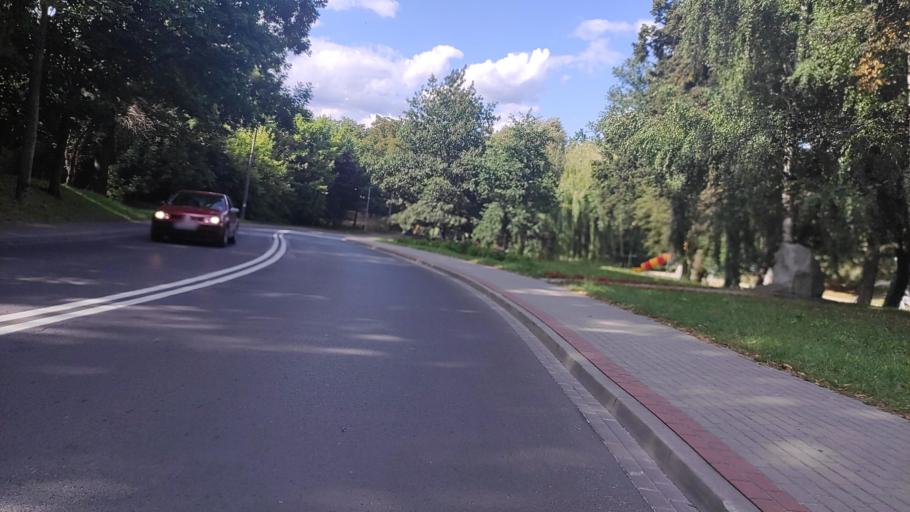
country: PL
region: Greater Poland Voivodeship
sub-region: Powiat poznanski
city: Swarzedz
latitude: 52.4066
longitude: 17.0742
